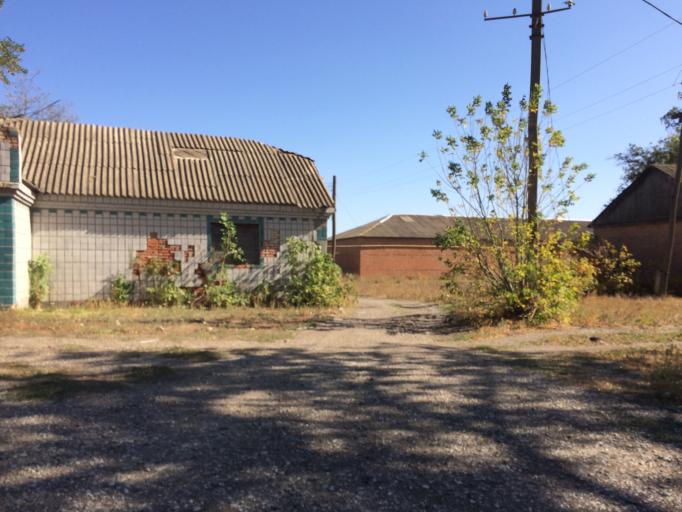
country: RU
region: Rostov
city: Gigant
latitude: 46.5155
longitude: 41.1883
